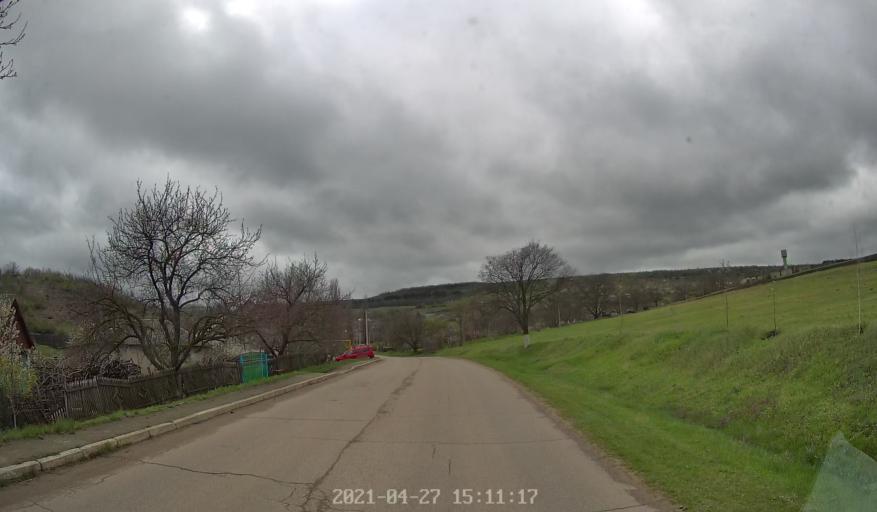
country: MD
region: Chisinau
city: Vadul lui Voda
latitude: 47.0330
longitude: 29.0285
